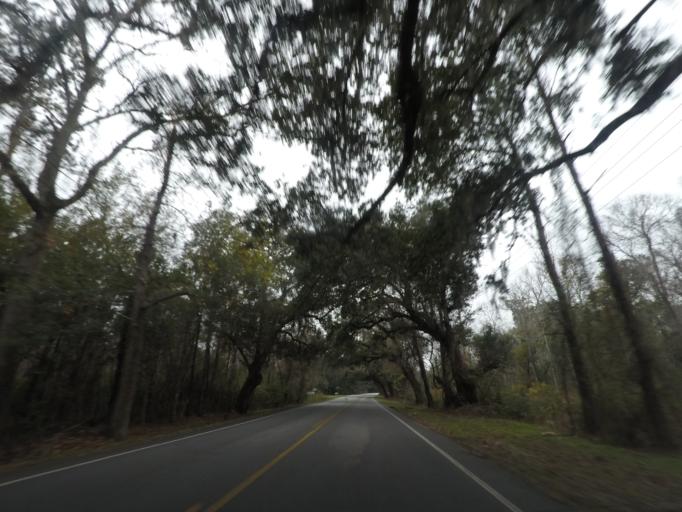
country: US
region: South Carolina
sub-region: Charleston County
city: Seabrook Island
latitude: 32.5774
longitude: -80.3187
